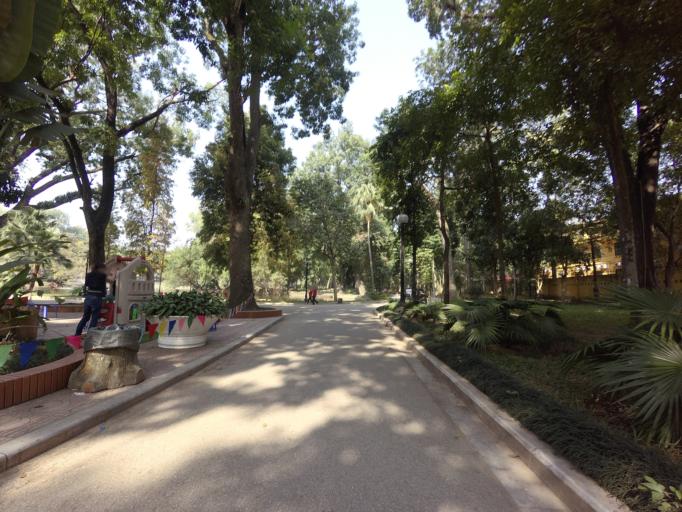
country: VN
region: Ha Noi
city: Hanoi
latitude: 21.0395
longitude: 105.8317
